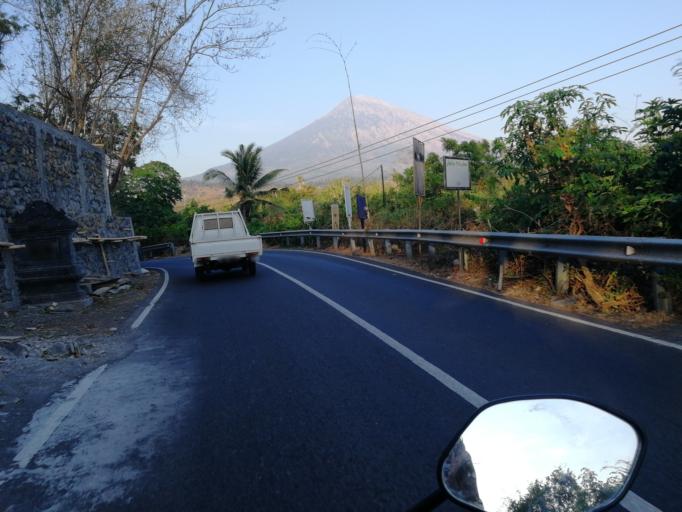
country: ID
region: Bali
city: Biaslantang Kaler
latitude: -8.3370
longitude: 115.6231
